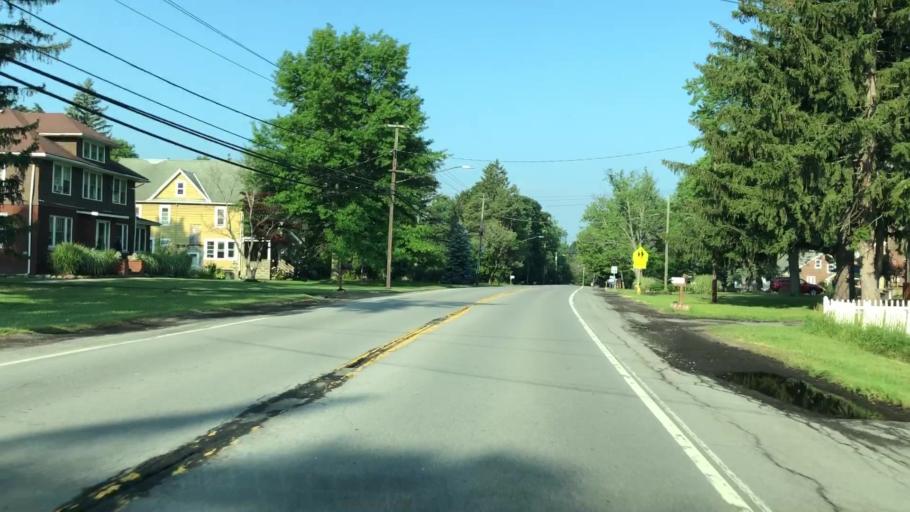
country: US
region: New York
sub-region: Erie County
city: Orchard Park
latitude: 42.8315
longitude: -78.7252
